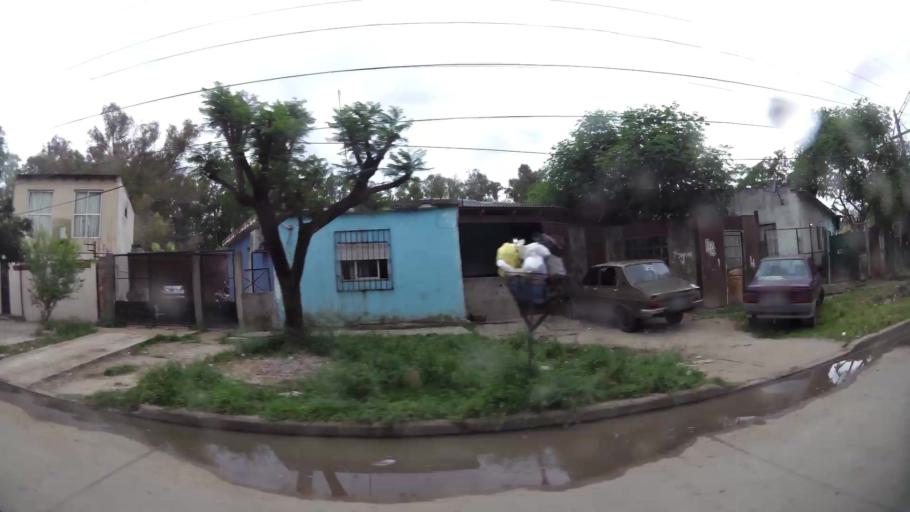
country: AR
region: Buenos Aires
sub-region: Partido de Zarate
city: Zarate
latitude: -34.0898
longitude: -59.0470
